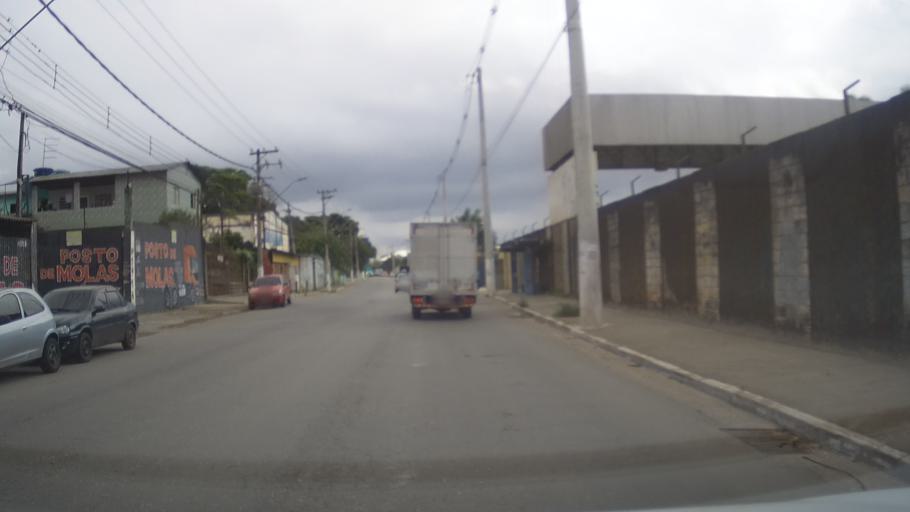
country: BR
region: Sao Paulo
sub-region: Aruja
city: Aruja
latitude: -23.4090
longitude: -46.4088
